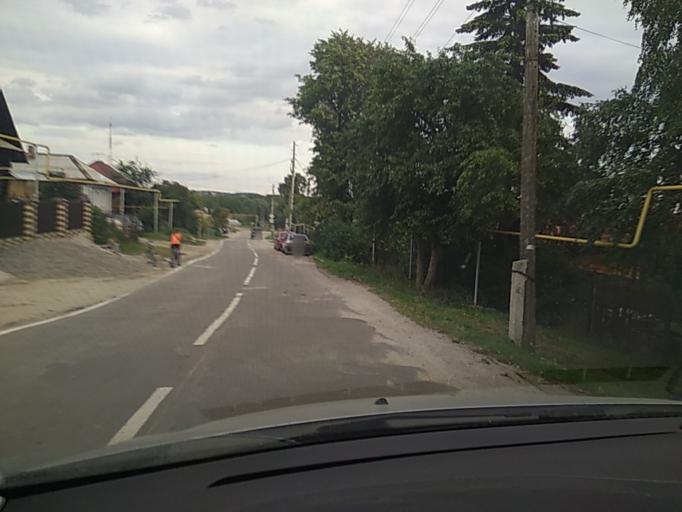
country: RU
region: Chelyabinsk
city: Kyshtym
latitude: 55.6976
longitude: 60.5307
